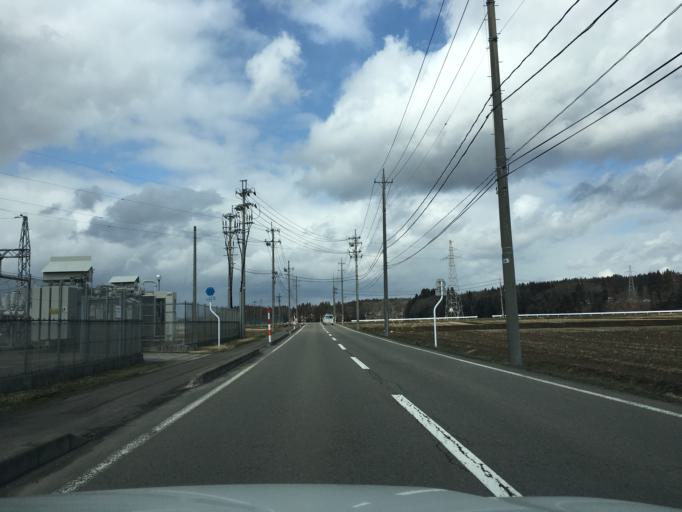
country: JP
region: Akita
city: Takanosu
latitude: 40.1250
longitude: 140.3657
